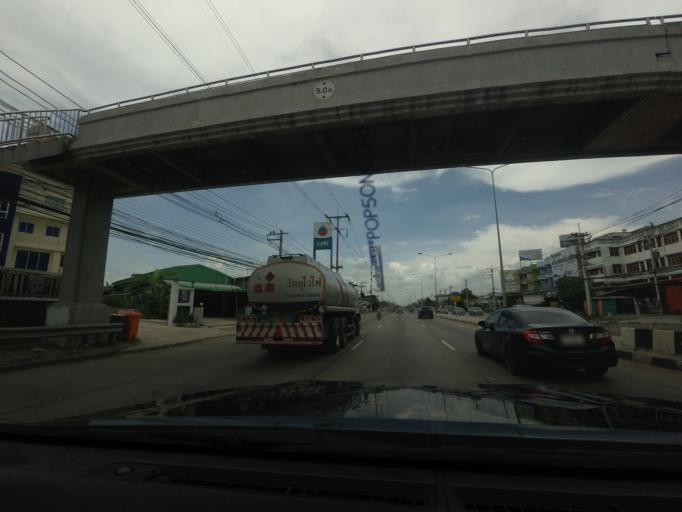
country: TH
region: Nakhon Pathom
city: Nakhon Pathom
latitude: 13.8416
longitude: 100.0272
